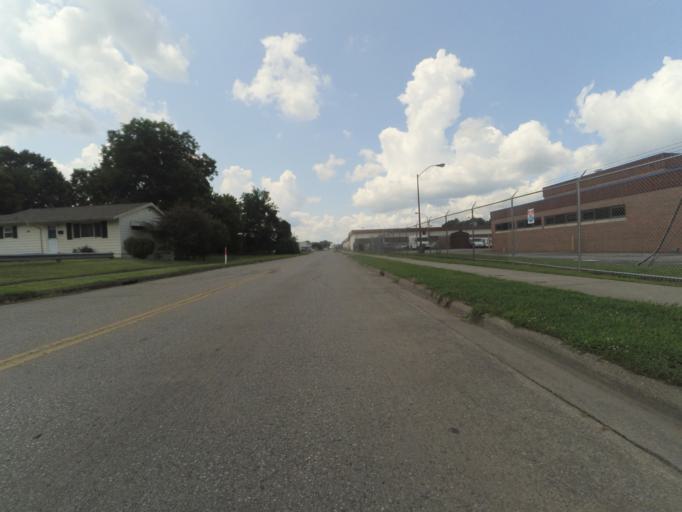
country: US
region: West Virginia
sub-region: Cabell County
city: Huntington
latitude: 38.4162
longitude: -82.4726
